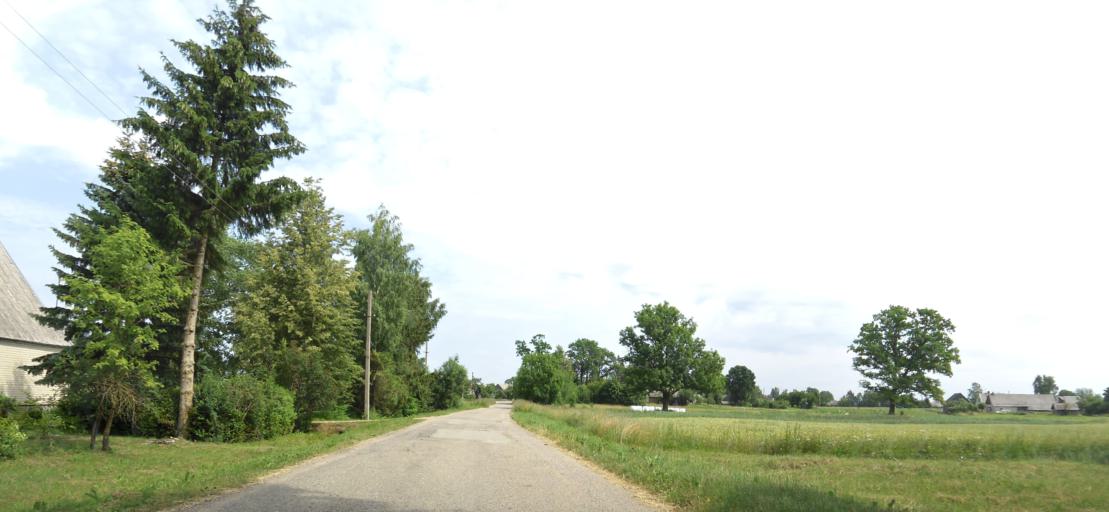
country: LT
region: Panevezys
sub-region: Birzai
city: Birzai
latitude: 56.3269
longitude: 24.7059
